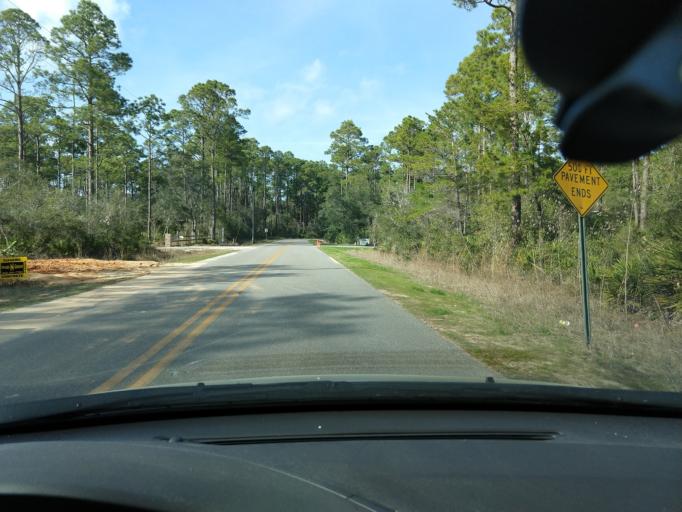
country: US
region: Florida
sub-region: Walton County
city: Seaside
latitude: 30.3757
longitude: -86.1242
